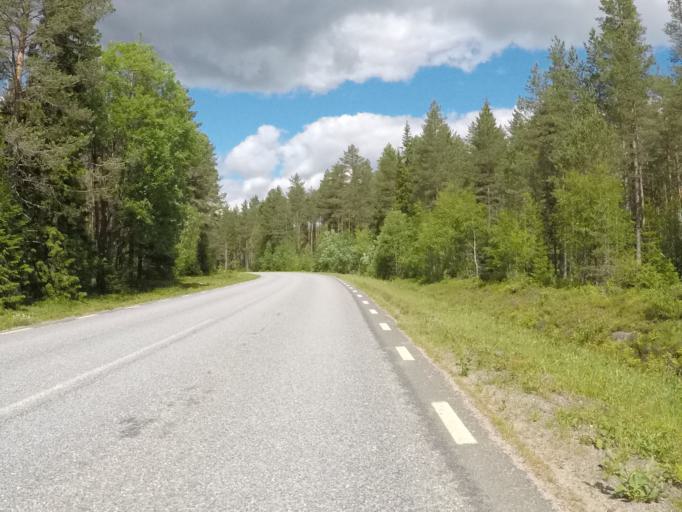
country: SE
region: Vaesterbotten
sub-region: Robertsfors Kommun
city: Robertsfors
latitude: 63.9776
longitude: 20.8104
